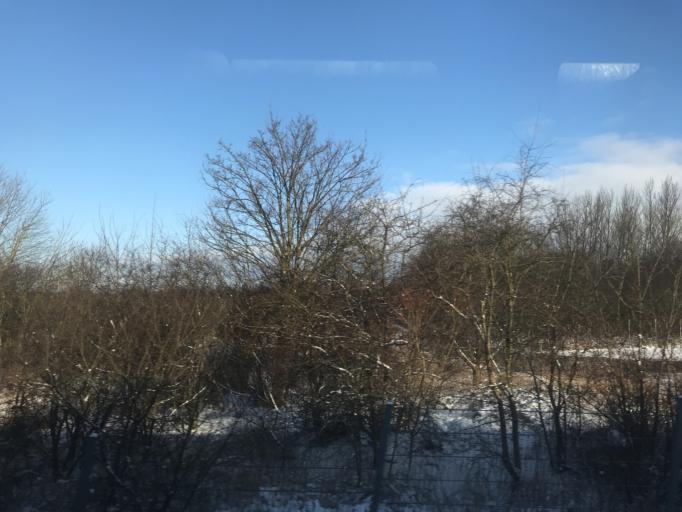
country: SE
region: Skane
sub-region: Lunds Kommun
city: Lund
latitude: 55.6926
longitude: 13.1680
